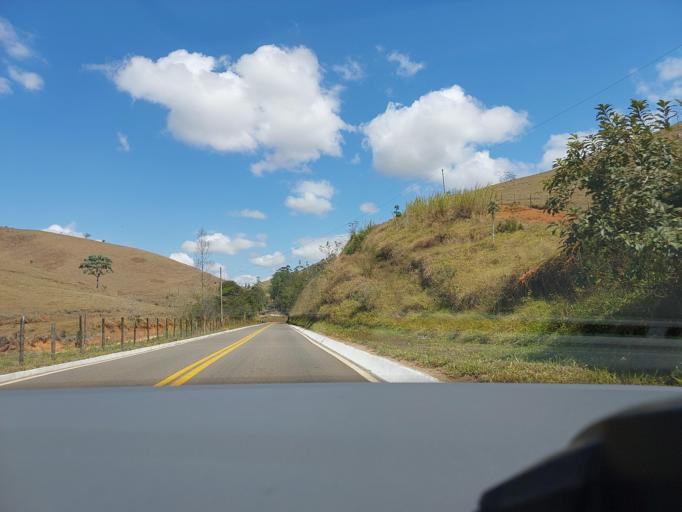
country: BR
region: Minas Gerais
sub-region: Muriae
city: Muriae
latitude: -21.0637
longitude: -42.5028
